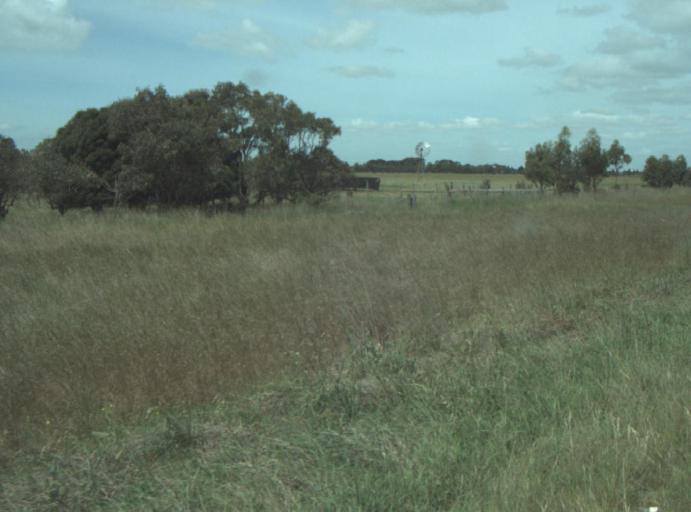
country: AU
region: Victoria
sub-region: Wyndham
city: Little River
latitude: -38.0039
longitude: 144.4683
